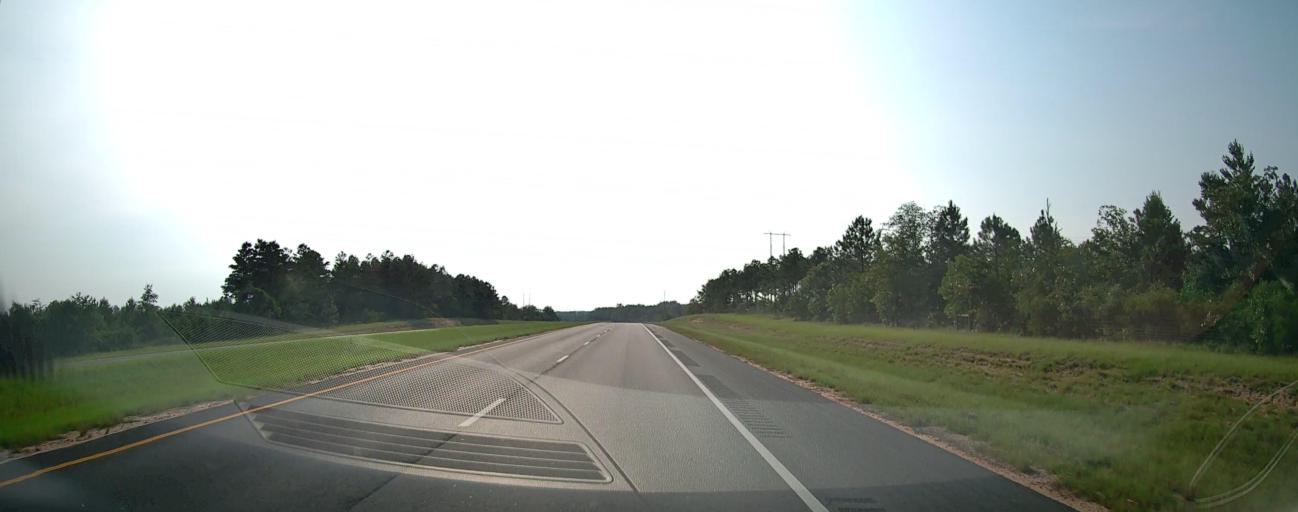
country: US
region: Georgia
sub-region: Taylor County
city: Butler
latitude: 32.5901
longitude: -84.3743
